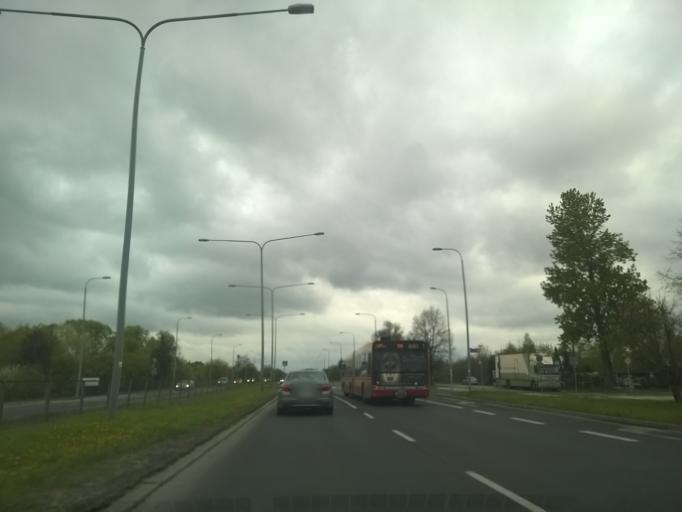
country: PL
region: Masovian Voivodeship
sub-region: Warszawa
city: Wilanow
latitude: 52.1472
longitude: 21.0933
